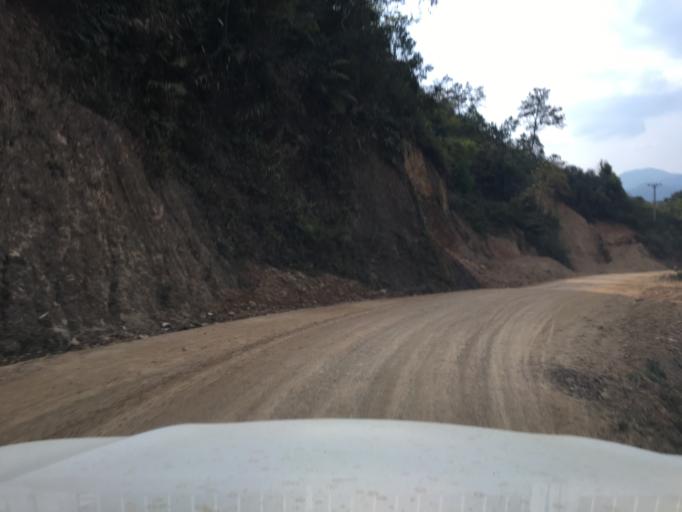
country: LA
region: Houaphan
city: Huameung
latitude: 20.2107
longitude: 103.8702
